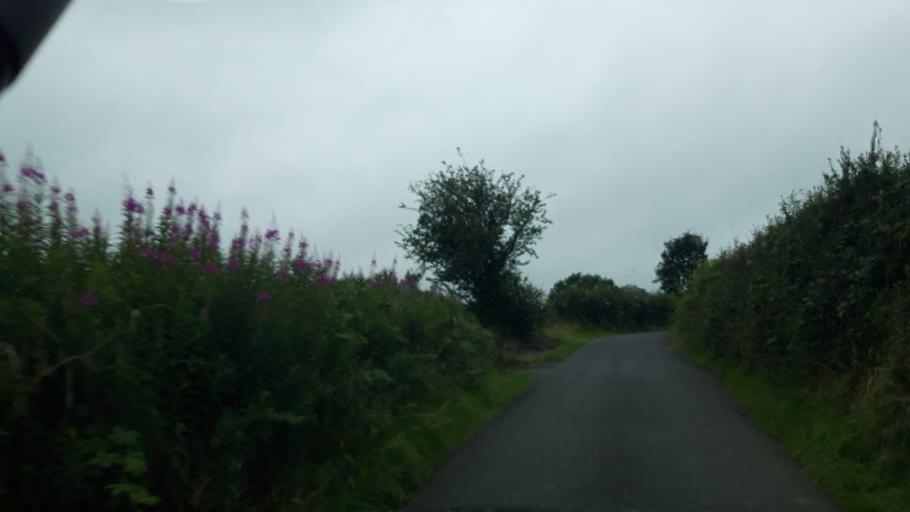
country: IE
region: Leinster
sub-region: Kilkenny
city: Callan
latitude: 52.6394
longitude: -7.5080
